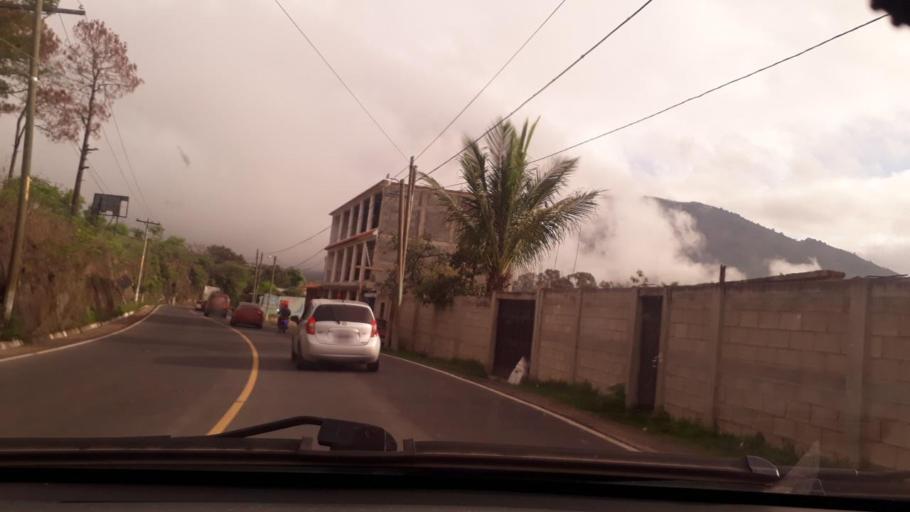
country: GT
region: Jalapa
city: Jalapa
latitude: 14.6562
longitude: -89.9999
